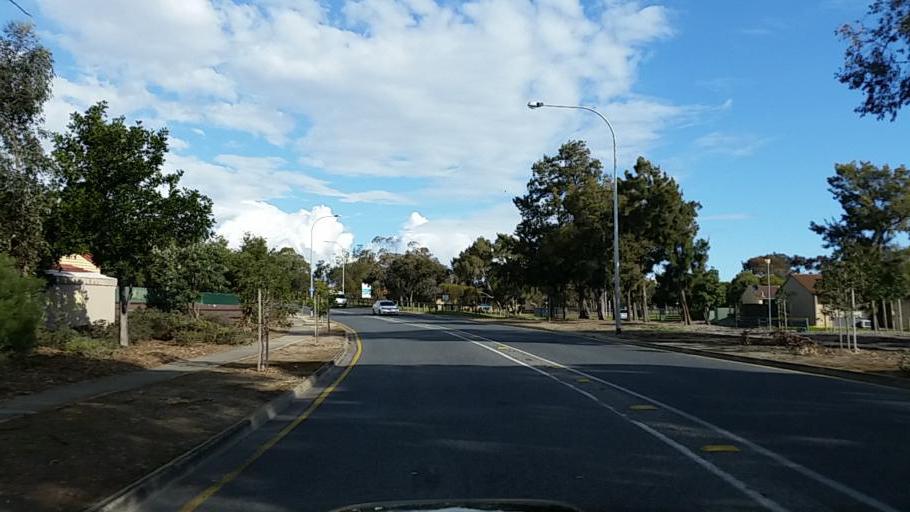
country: AU
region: South Australia
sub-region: Charles Sturt
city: West Lakes Shore
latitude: -34.8537
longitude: 138.4931
